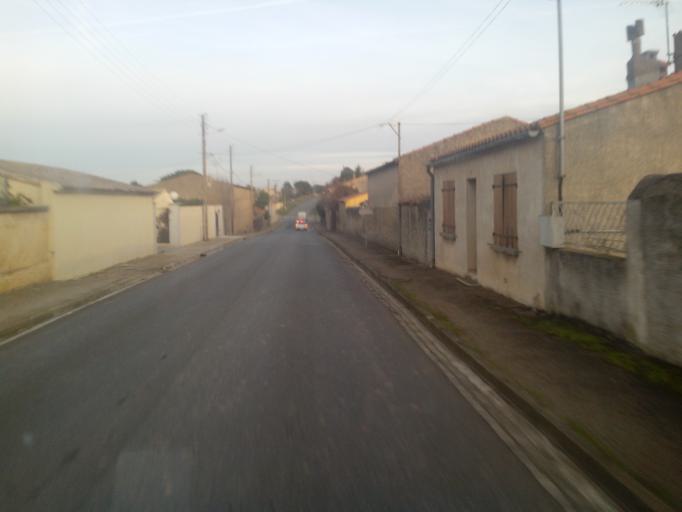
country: FR
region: Languedoc-Roussillon
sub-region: Departement de l'Aude
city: Capendu
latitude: 43.2038
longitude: 2.5447
